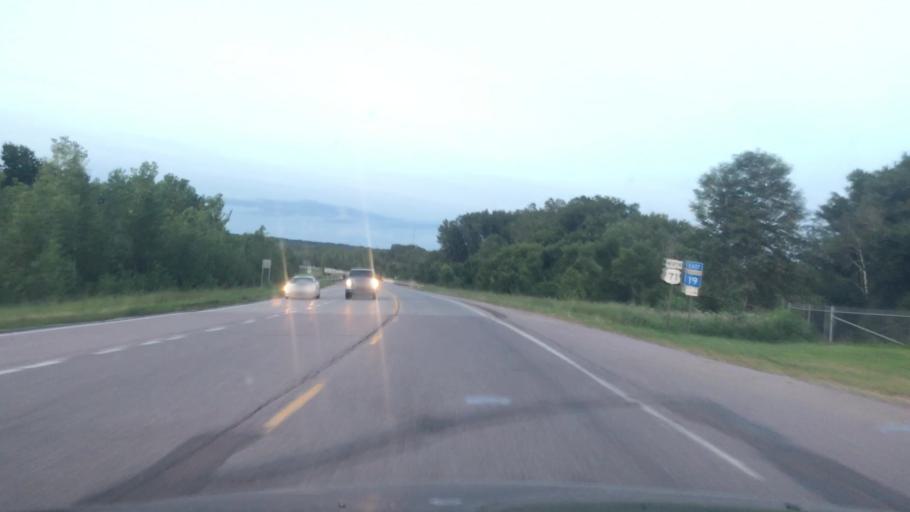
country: US
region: Minnesota
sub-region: Redwood County
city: Redwood Falls
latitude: 44.5403
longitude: -95.0060
